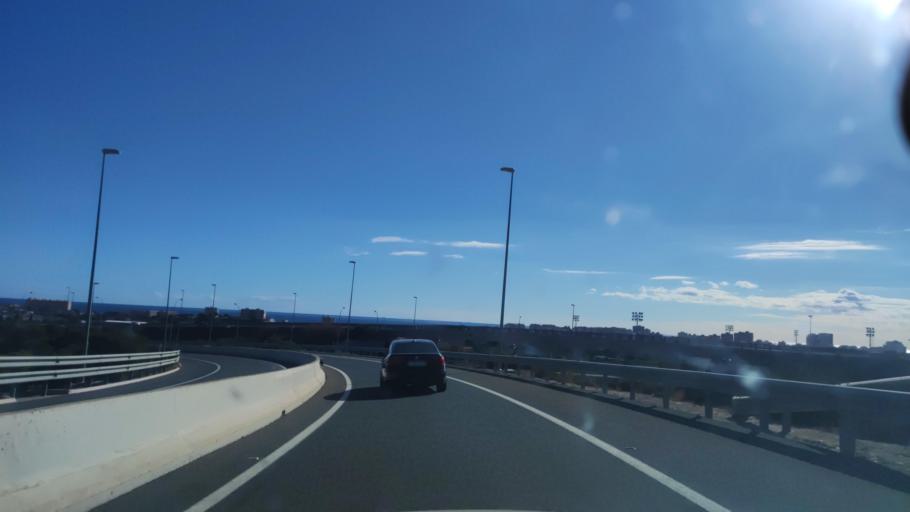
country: ES
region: Valencia
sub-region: Provincia de Alicante
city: el Campello
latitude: 38.4387
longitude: -0.4047
